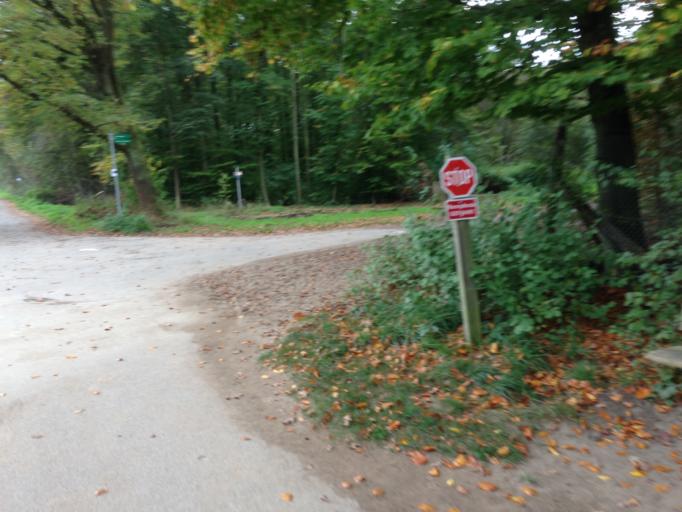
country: DE
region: North Rhine-Westphalia
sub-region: Regierungsbezirk Koln
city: Eil
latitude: 50.8943
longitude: 7.0965
